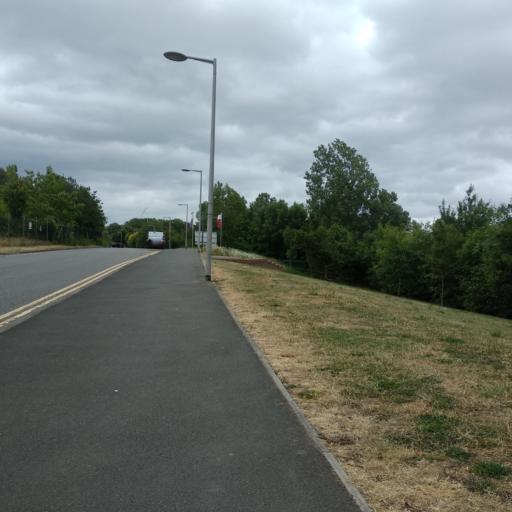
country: GB
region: England
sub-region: Kent
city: Ashford
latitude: 51.1530
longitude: 0.8550
